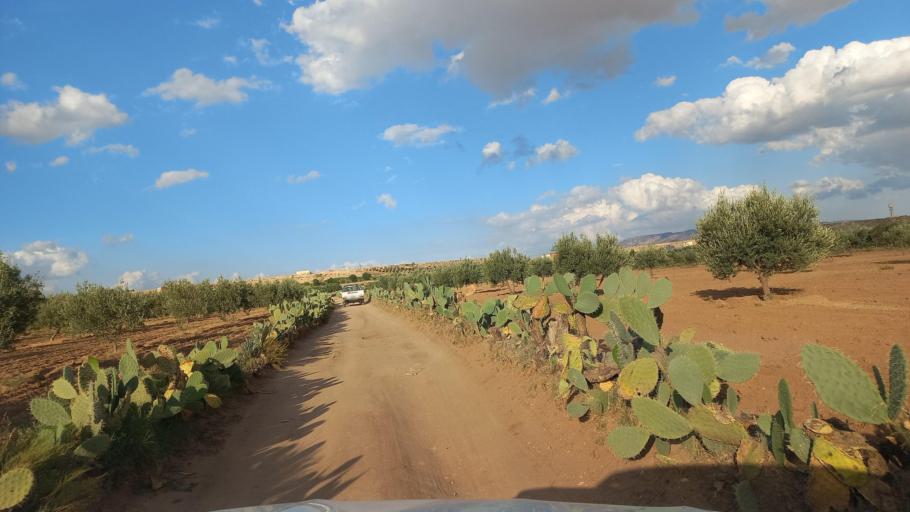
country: TN
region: Al Qasrayn
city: Sbiba
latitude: 35.3835
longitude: 9.0547
